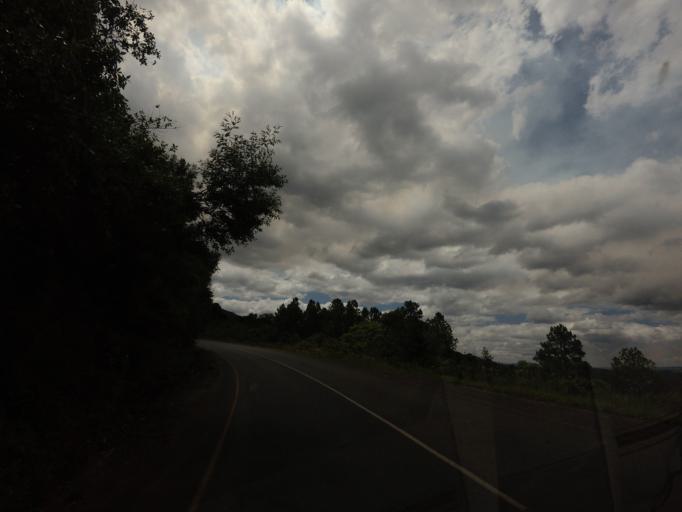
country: ZA
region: Mpumalanga
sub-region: Ehlanzeni District
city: Graksop
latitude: -24.9349
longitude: 30.8132
